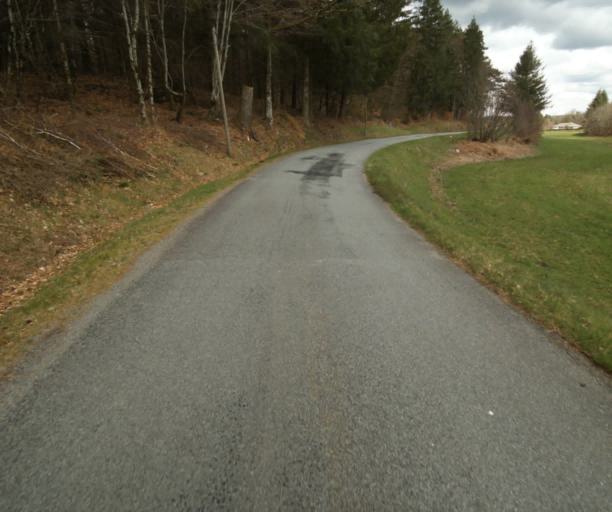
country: FR
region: Limousin
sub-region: Departement de la Correze
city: Correze
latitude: 45.3243
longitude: 1.9544
